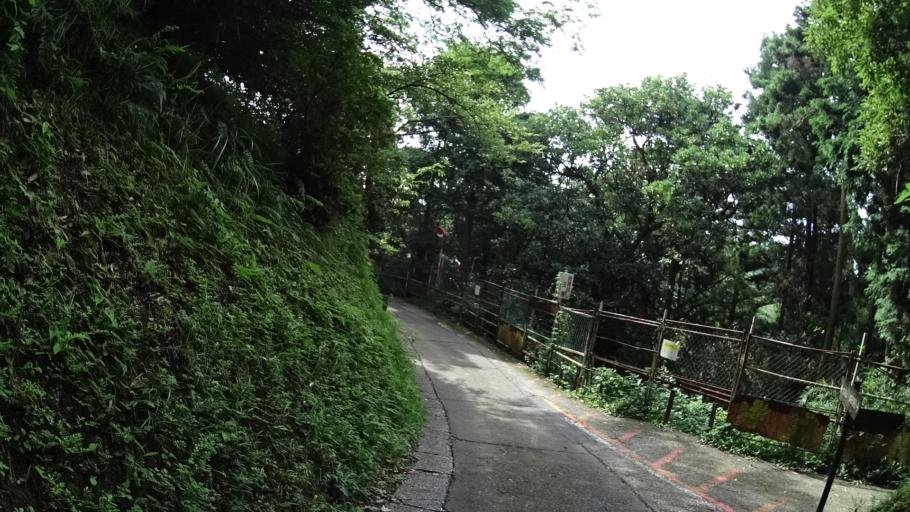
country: JP
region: Kanagawa
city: Yokosuka
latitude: 35.2790
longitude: 139.6407
